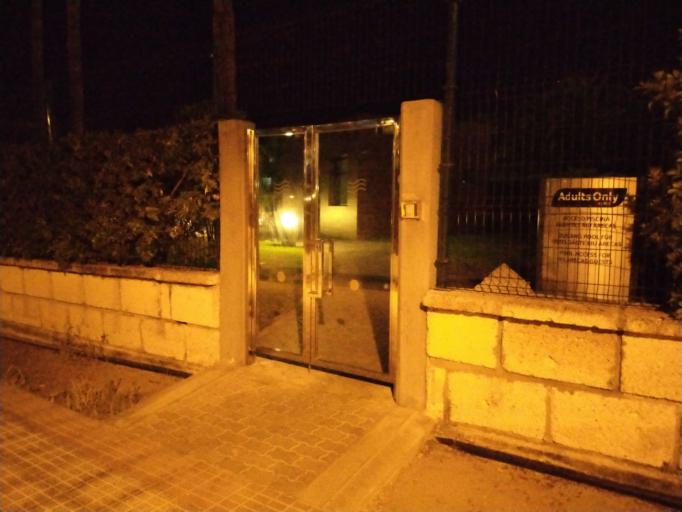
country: ES
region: Canary Islands
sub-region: Provincia de Santa Cruz de Tenerife
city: Playa de las Americas
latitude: 28.0939
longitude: -16.7470
